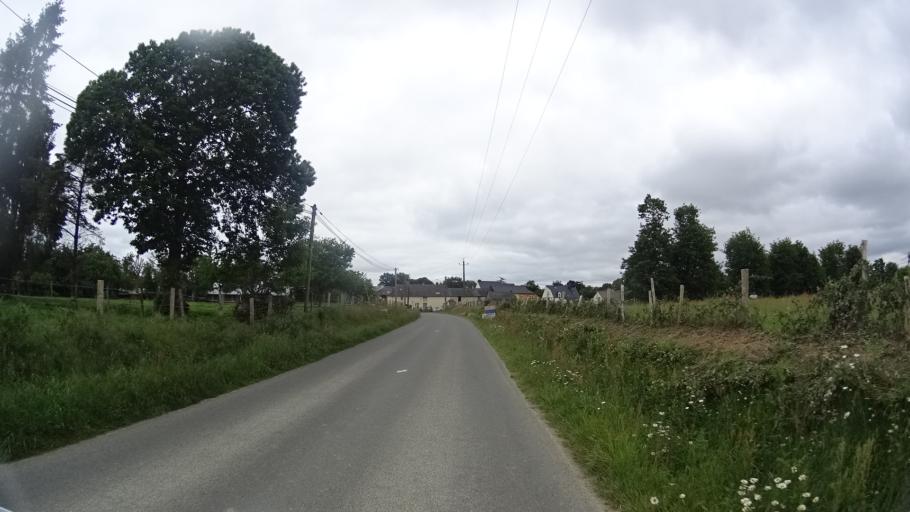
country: FR
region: Brittany
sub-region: Departement d'Ille-et-Vilaine
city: Romille
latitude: 48.2094
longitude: -1.8951
